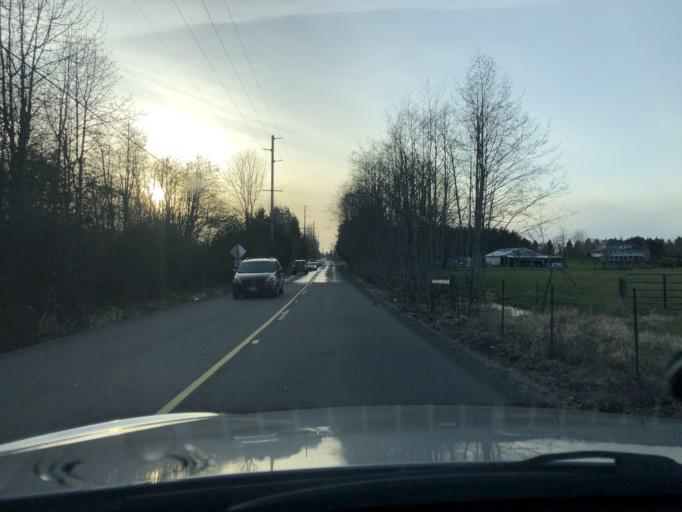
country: US
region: Washington
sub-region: Pierce County
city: Bonney Lake
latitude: 47.2211
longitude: -122.1237
